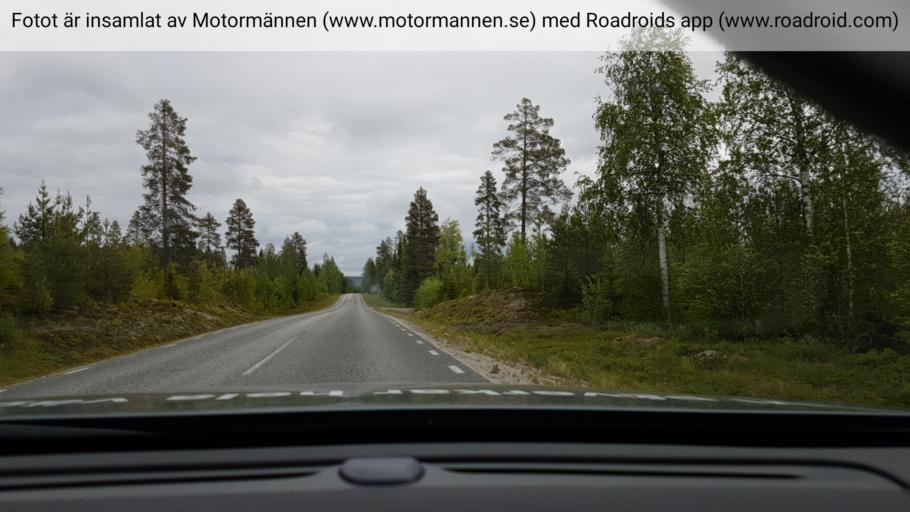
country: SE
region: Vaesterbotten
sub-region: Asele Kommun
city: Insjon
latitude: 64.3290
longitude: 17.7306
